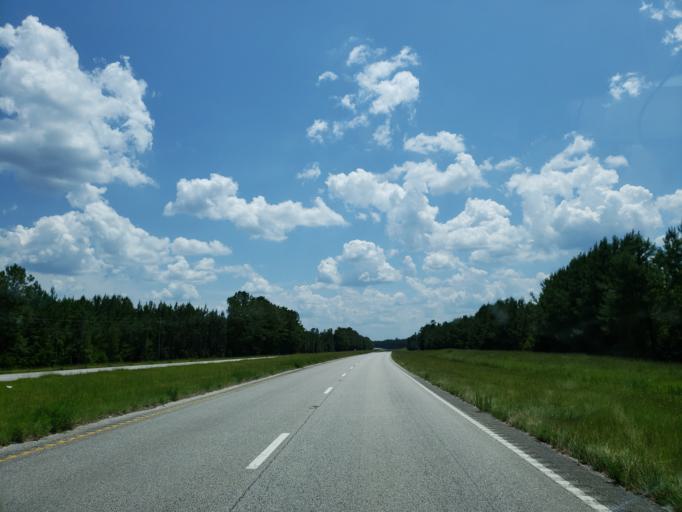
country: US
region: Mississippi
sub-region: Greene County
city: Leakesville
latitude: 31.3377
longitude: -88.5050
